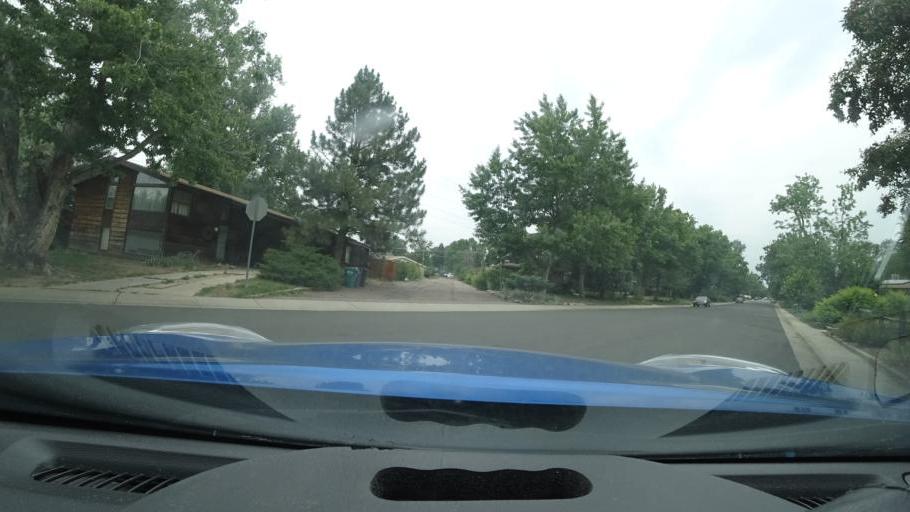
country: US
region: Colorado
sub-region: Arapahoe County
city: Glendale
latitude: 39.6913
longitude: -104.9184
